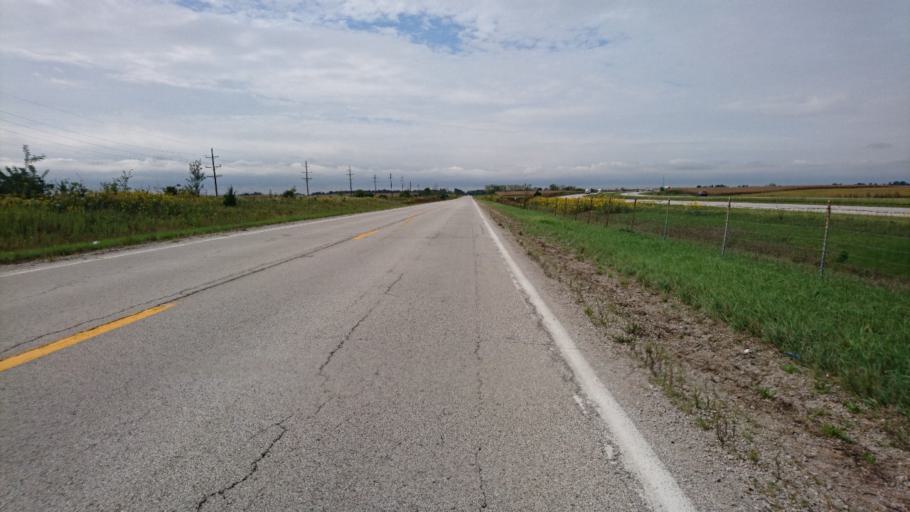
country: US
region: Illinois
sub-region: Livingston County
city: Odell
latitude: 41.0293
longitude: -88.5011
